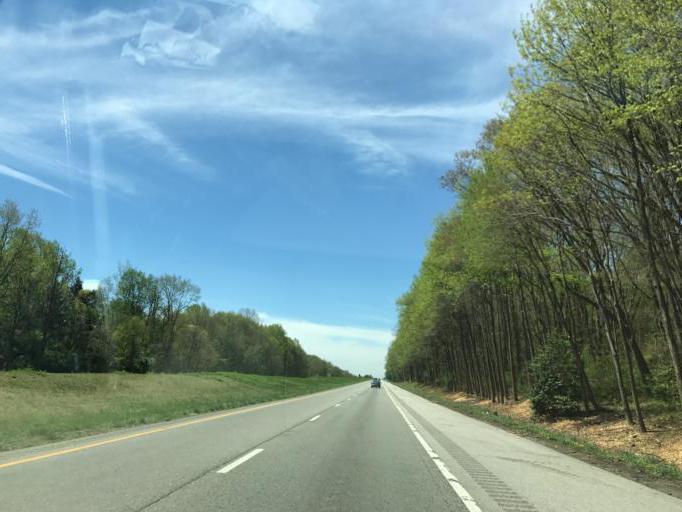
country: US
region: Delaware
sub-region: New Castle County
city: Bellefonte
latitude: 39.7904
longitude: -75.4926
